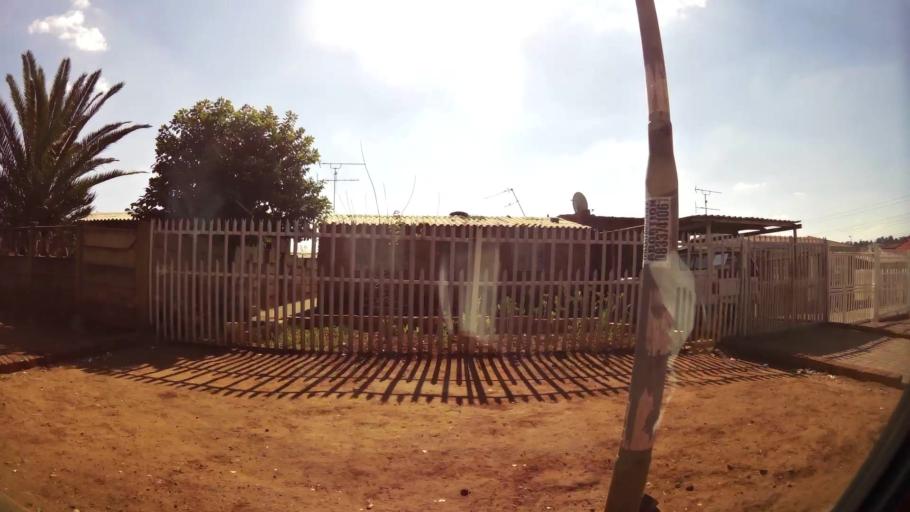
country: ZA
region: Gauteng
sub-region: City of Johannesburg Metropolitan Municipality
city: Soweto
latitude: -26.2402
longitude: 27.8873
